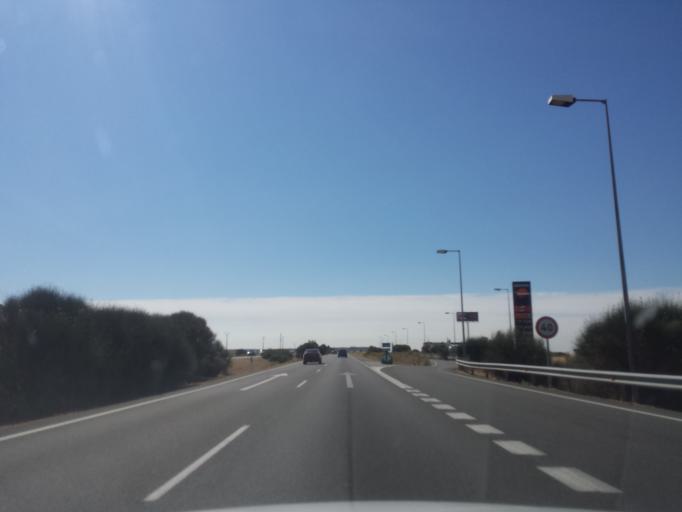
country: ES
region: Castille and Leon
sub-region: Provincia de Valladolid
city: Vega de Valdetronco
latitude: 41.5787
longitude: -5.1022
